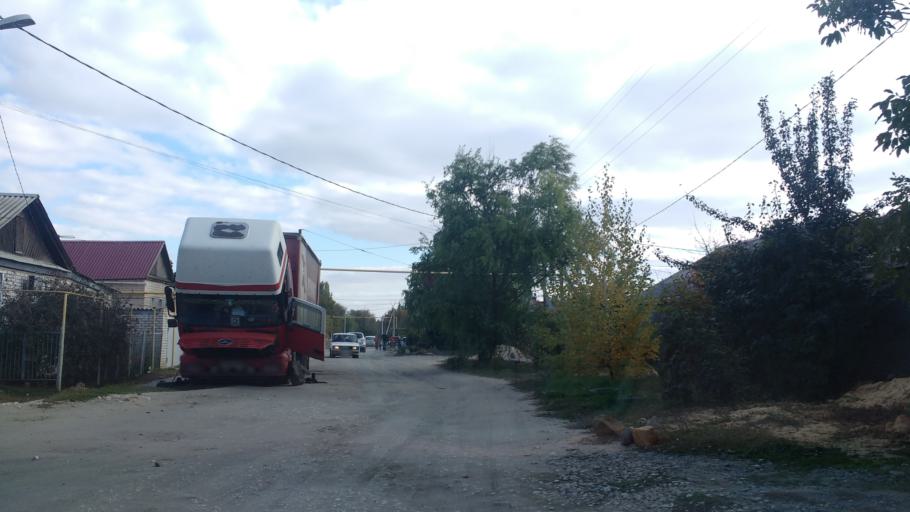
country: RU
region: Volgograd
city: Volgograd
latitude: 48.7562
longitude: 44.5440
